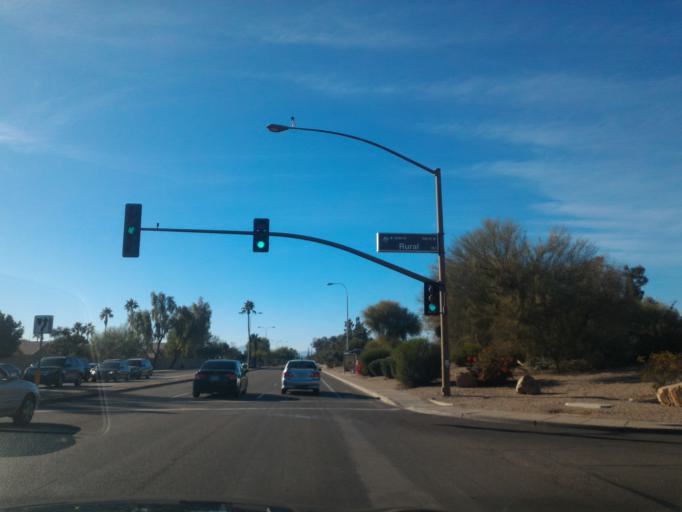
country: US
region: Arizona
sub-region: Maricopa County
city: Guadalupe
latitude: 33.3056
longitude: -111.9287
